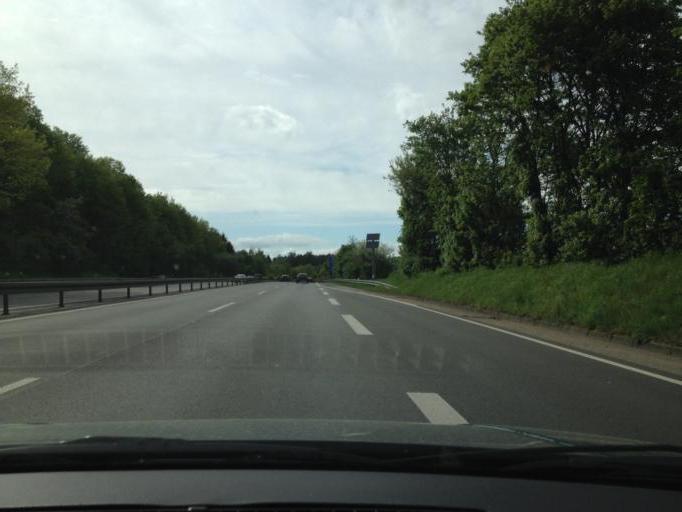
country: DE
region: Saarland
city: Kirkel
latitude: 49.3113
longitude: 7.2495
